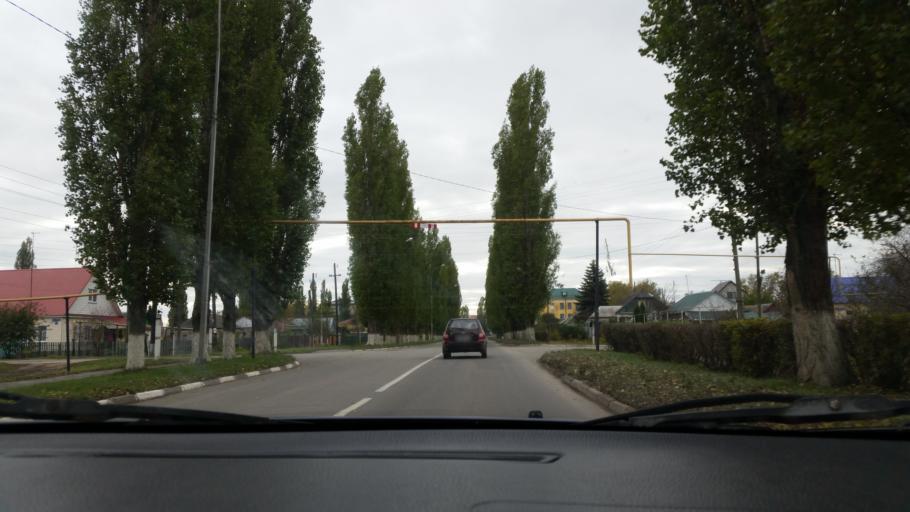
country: RU
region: Lipetsk
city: Gryazi
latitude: 52.4804
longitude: 39.9520
